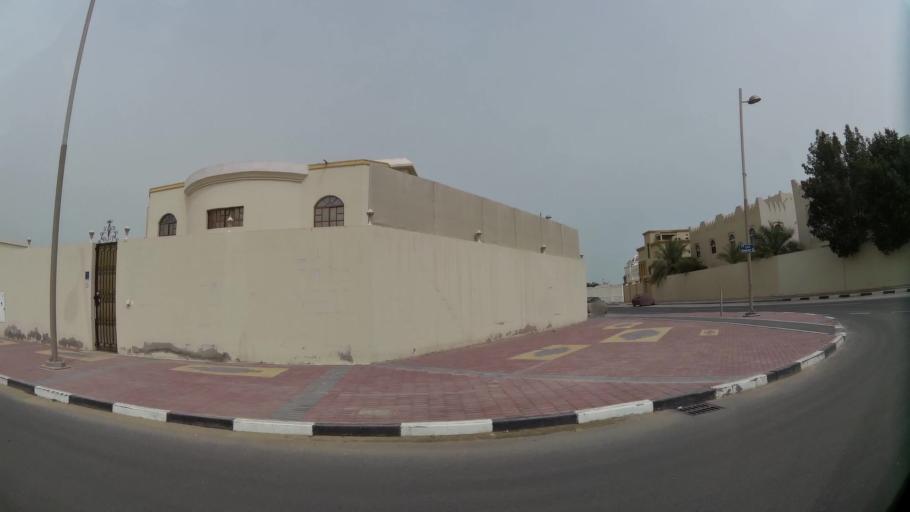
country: QA
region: Baladiyat ad Dawhah
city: Doha
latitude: 25.2342
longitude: 51.5422
